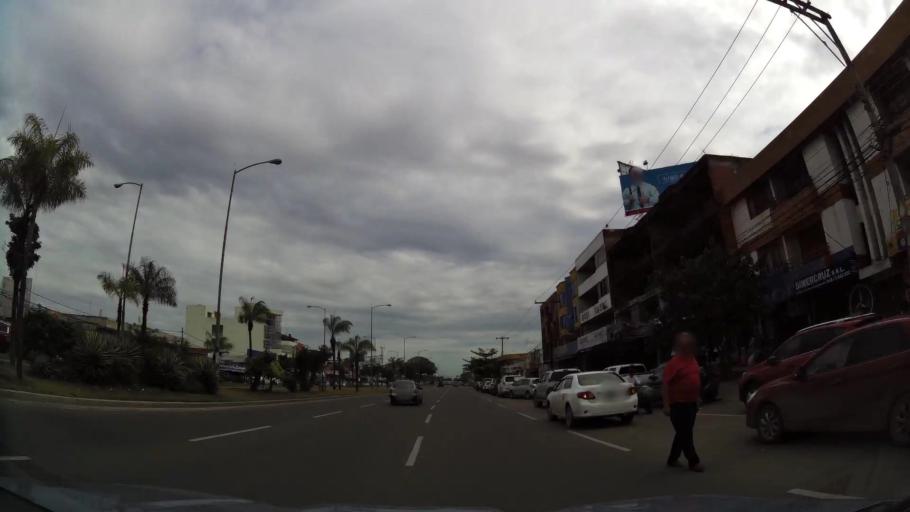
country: BO
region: Santa Cruz
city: Santa Cruz de la Sierra
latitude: -17.8019
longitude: -63.1972
